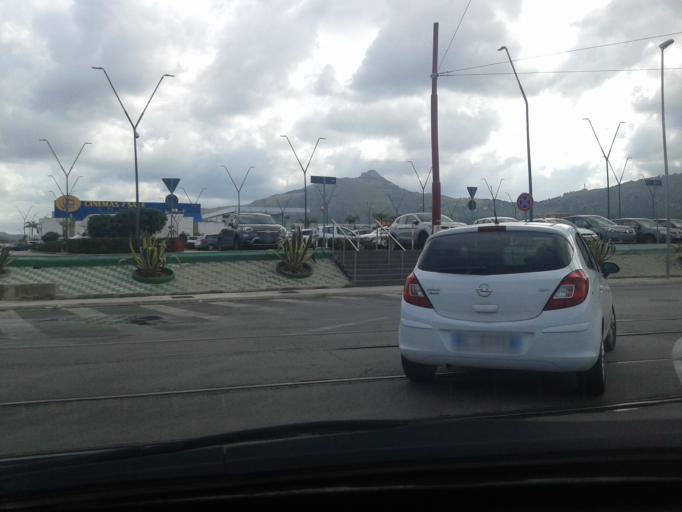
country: IT
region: Sicily
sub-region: Palermo
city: Ciaculli
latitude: 38.0914
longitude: 13.4104
